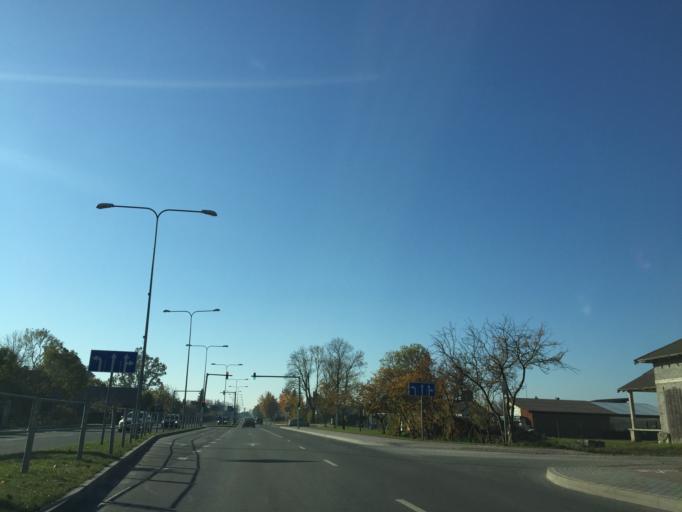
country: LT
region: Klaipedos apskritis
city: Kretinga
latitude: 55.8929
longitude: 21.2350
